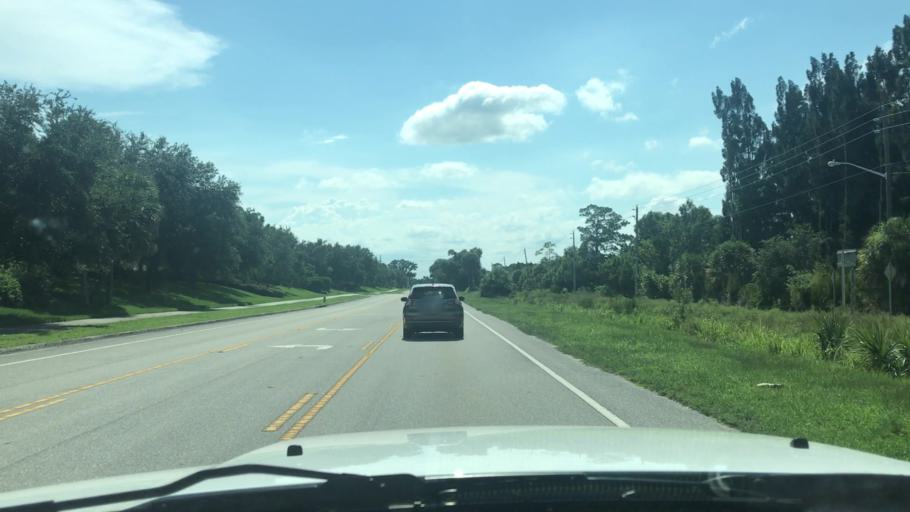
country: US
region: Florida
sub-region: Indian River County
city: Florida Ridge
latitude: 27.5722
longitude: -80.4085
